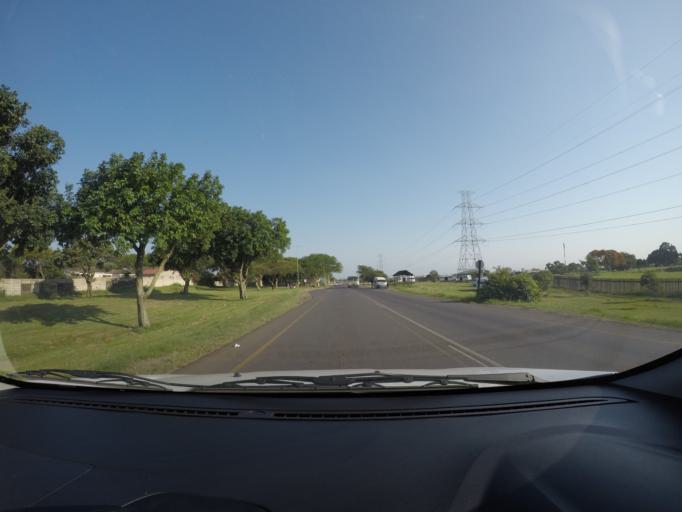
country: ZA
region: KwaZulu-Natal
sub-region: uThungulu District Municipality
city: Richards Bay
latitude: -28.7290
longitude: 32.0372
